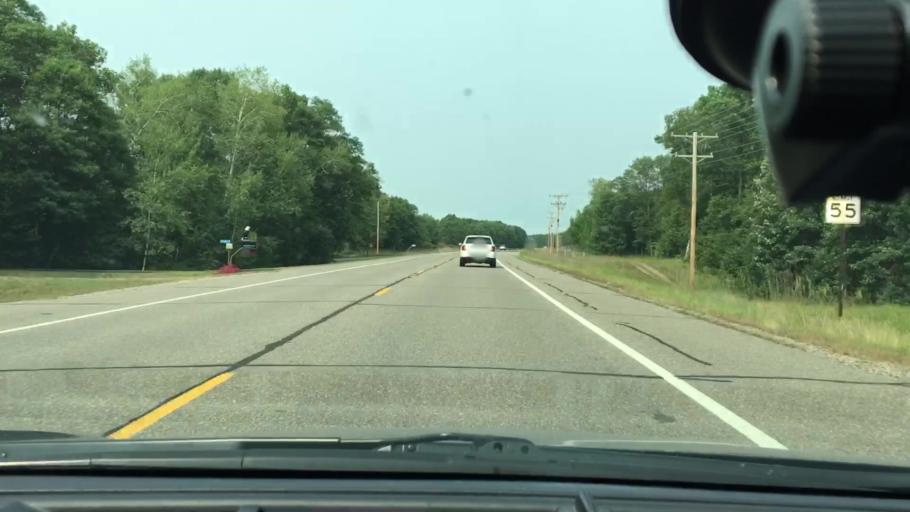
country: US
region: Minnesota
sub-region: Crow Wing County
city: Cross Lake
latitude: 46.5939
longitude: -94.1316
